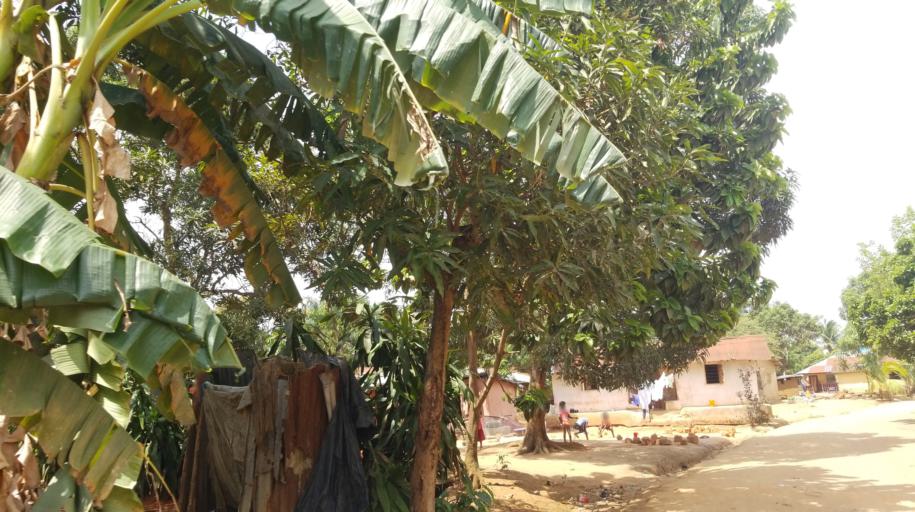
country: SL
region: Western Area
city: Waterloo
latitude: 8.3206
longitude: -13.0551
